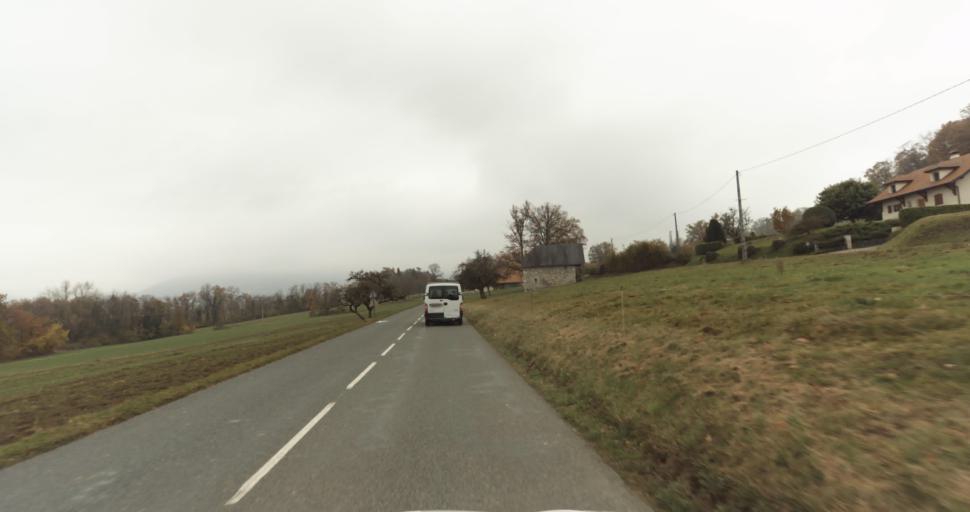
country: FR
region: Rhone-Alpes
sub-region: Departement de la Haute-Savoie
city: Cusy
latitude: 45.7888
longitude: 6.0120
